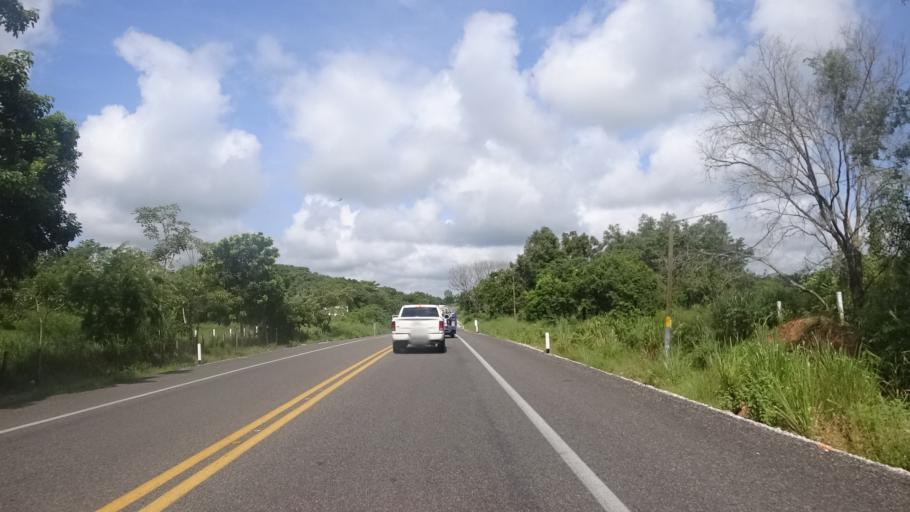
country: MX
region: Chiapas
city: Palenque
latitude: 17.5670
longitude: -92.0173
